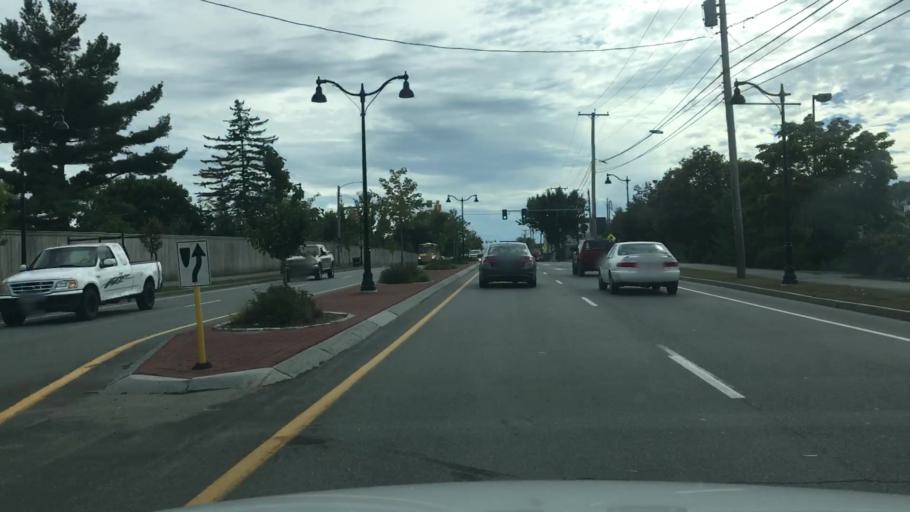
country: US
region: Maine
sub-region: Penobscot County
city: Bangor
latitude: 44.7940
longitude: -68.7752
